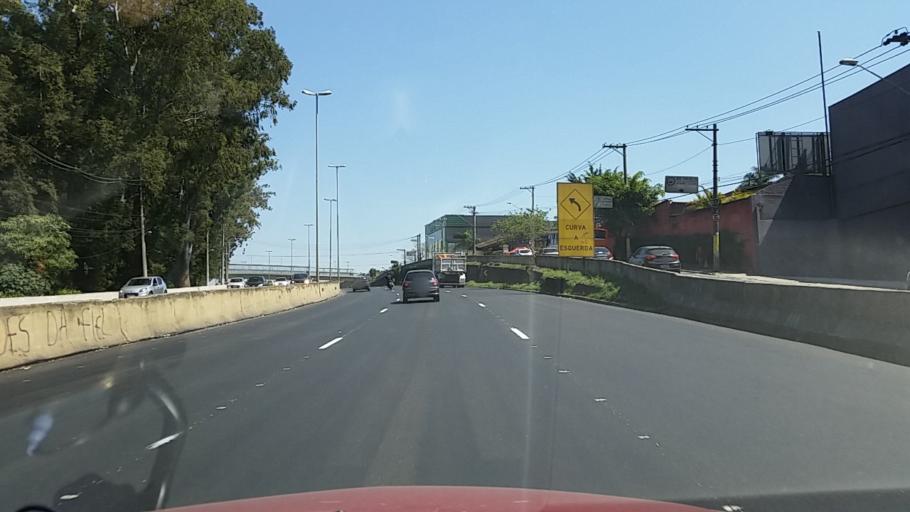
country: BR
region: Sao Paulo
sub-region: Taboao Da Serra
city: Taboao da Serra
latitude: -23.5849
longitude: -46.7442
